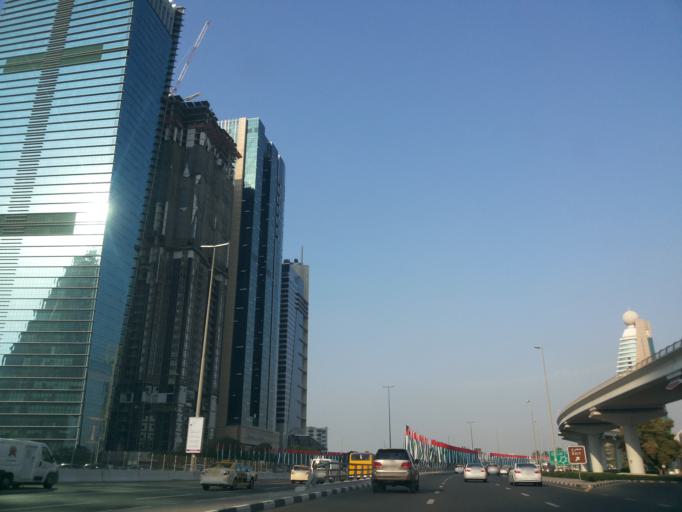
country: AE
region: Ash Shariqah
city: Sharjah
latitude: 25.2269
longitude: 55.2860
